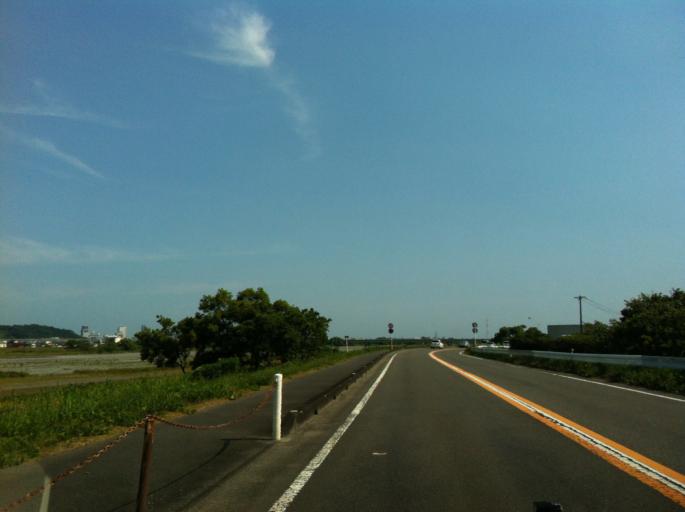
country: JP
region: Shizuoka
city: Shizuoka-shi
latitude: 34.9976
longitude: 138.3545
